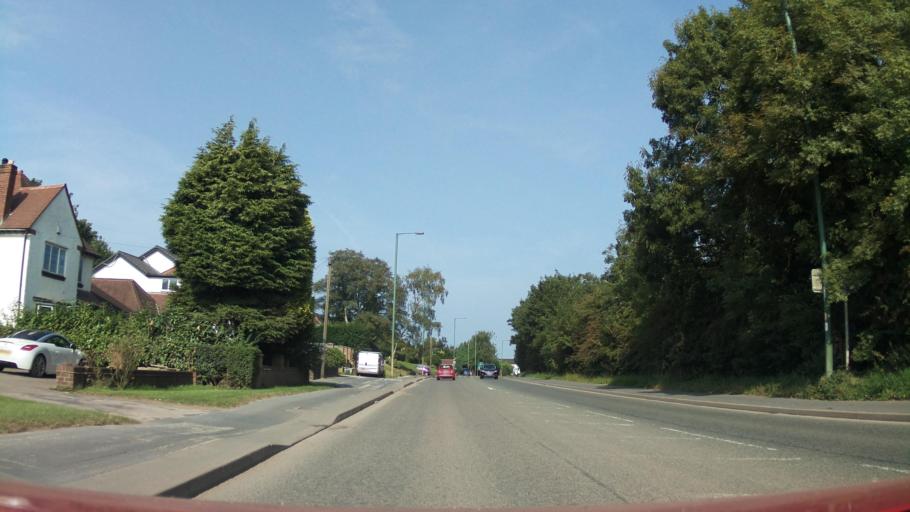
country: GB
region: England
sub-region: Walsall
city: Brownhills
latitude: 52.6338
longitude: -1.9139
